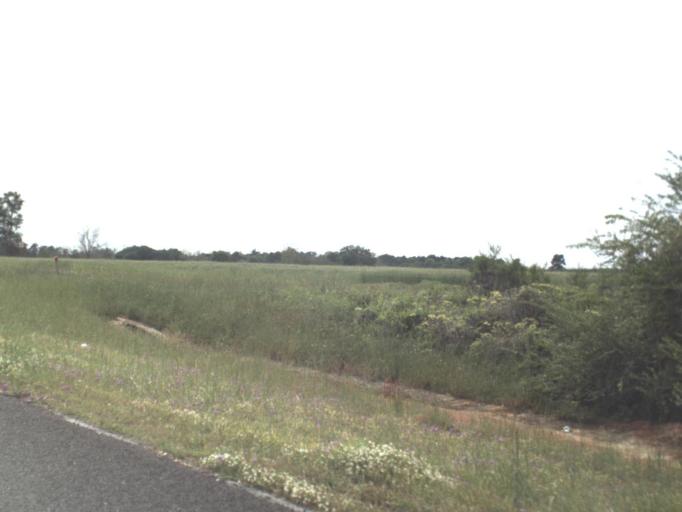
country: US
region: Florida
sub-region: Escambia County
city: Century
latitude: 30.9315
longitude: -87.2996
